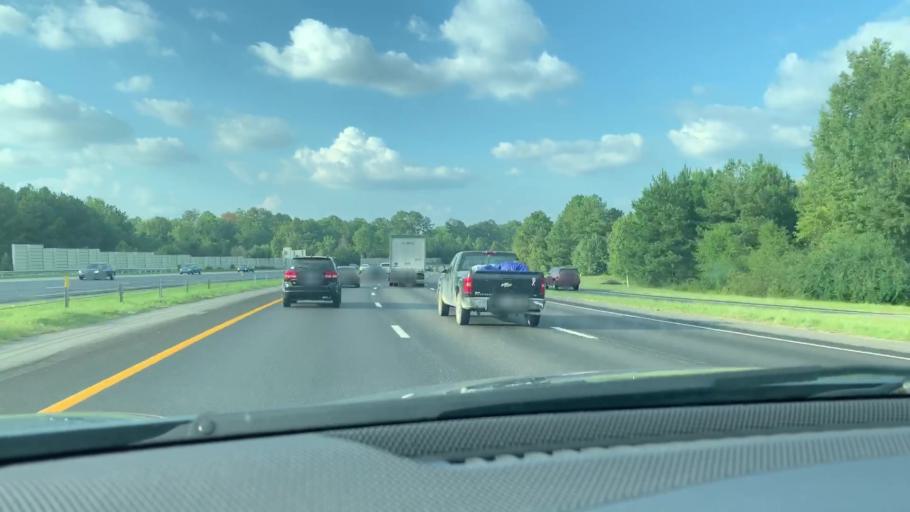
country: US
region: South Carolina
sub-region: Richland County
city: Forest Acres
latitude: 33.9971
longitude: -80.9595
